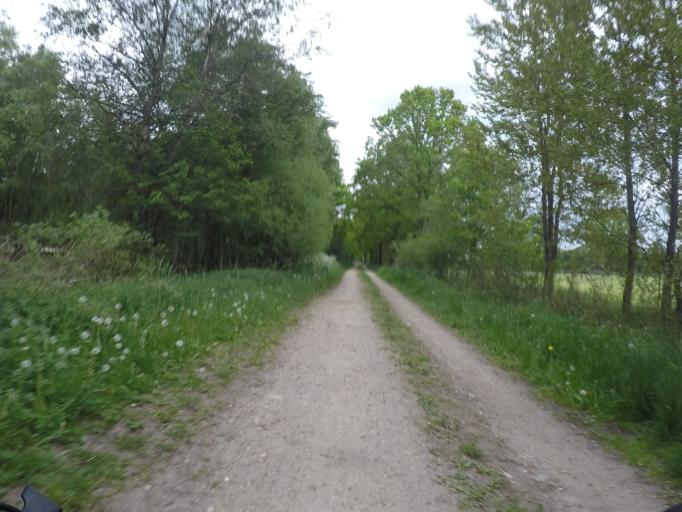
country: DE
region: Schleswig-Holstein
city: Henstedt-Ulzburg
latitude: 53.7638
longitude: 10.0150
